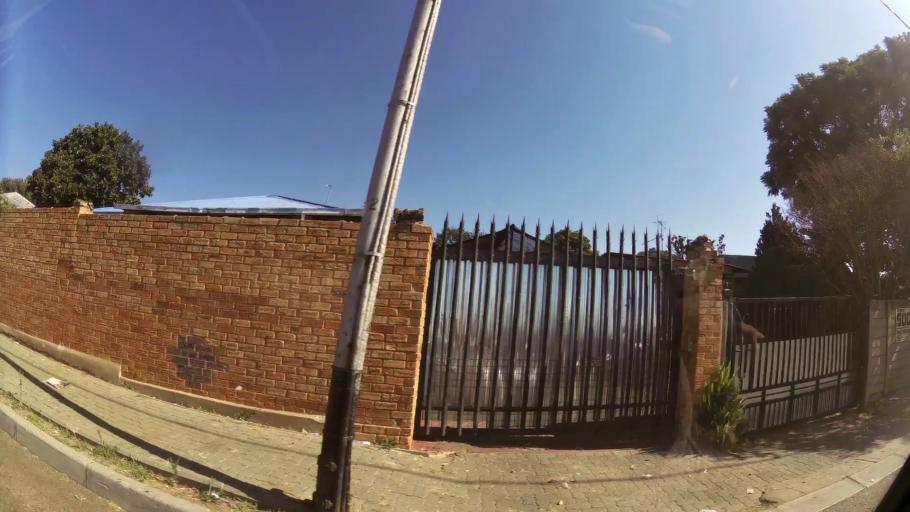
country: ZA
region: Gauteng
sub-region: City of Johannesburg Metropolitan Municipality
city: Johannesburg
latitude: -26.2496
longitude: 28.0917
